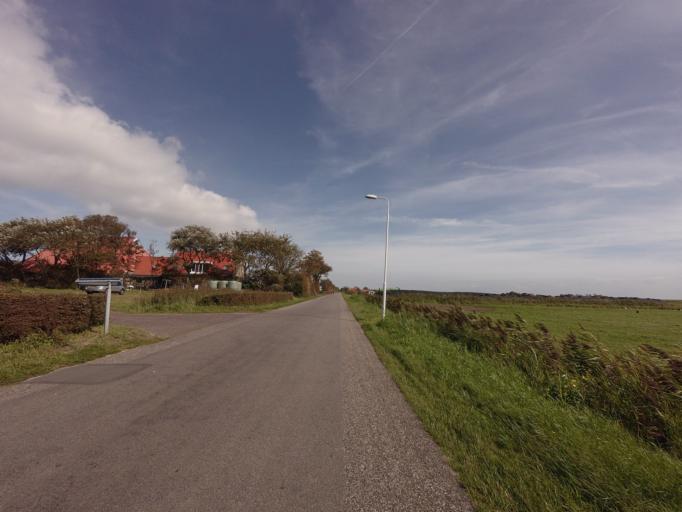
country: NL
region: Friesland
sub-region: Gemeente Ameland
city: Hollum
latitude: 53.4411
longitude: 5.7000
